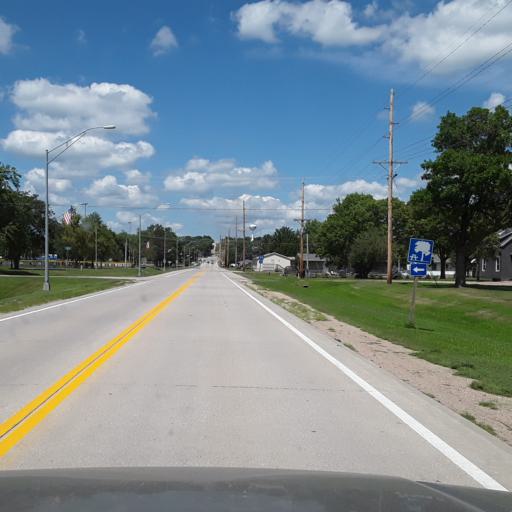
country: US
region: Nebraska
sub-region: Nance County
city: Genoa
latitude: 41.4419
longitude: -97.7346
